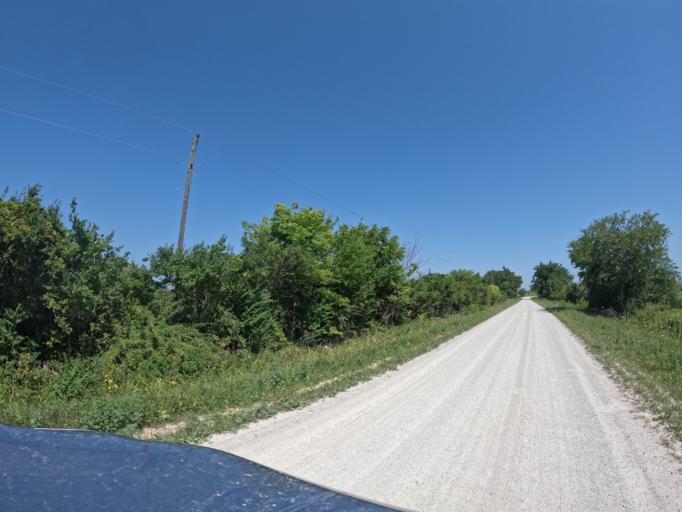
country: US
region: Iowa
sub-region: Henry County
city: Mount Pleasant
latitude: 40.9355
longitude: -91.5381
